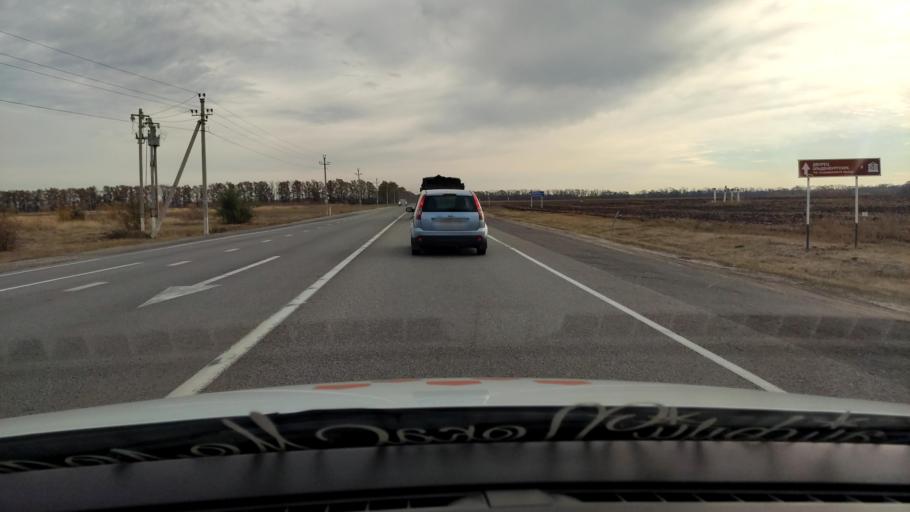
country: RU
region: Voronezj
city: Ramon'
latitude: 51.9298
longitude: 39.2260
